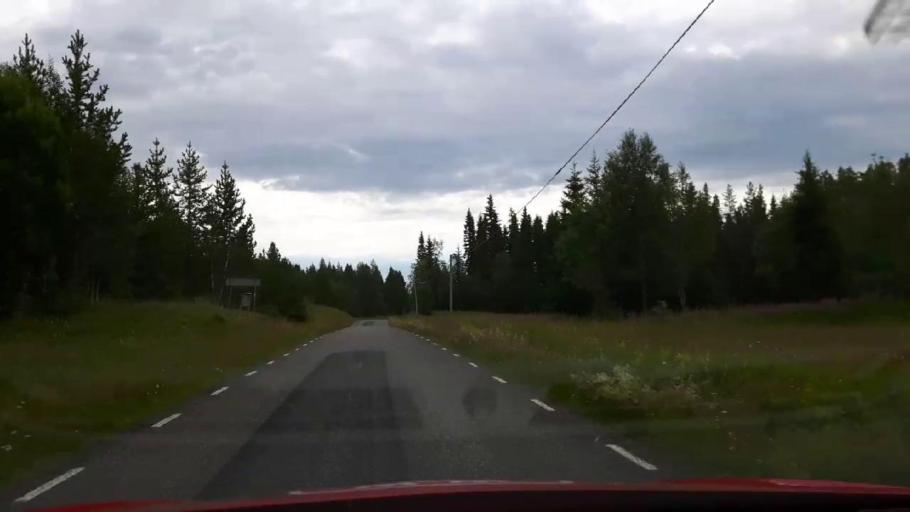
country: SE
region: Jaemtland
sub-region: OEstersunds Kommun
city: Lit
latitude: 63.3845
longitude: 15.0351
